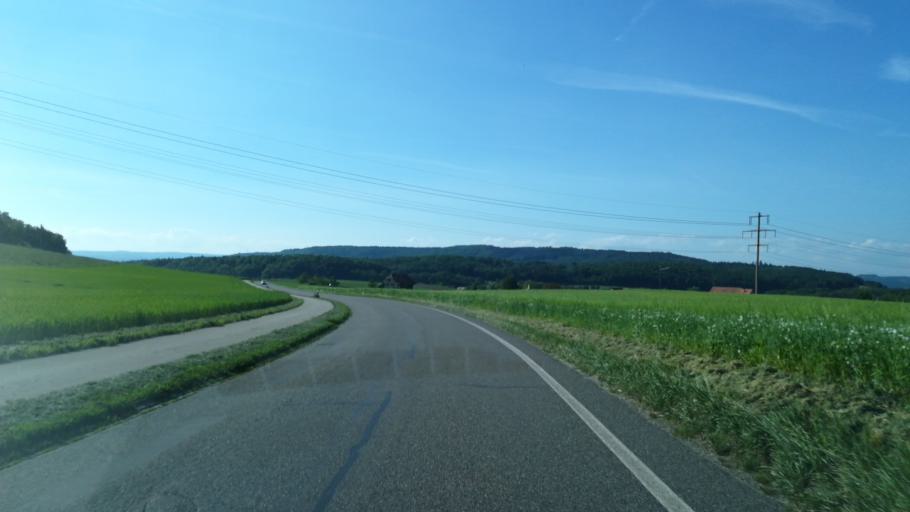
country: CH
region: Thurgau
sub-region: Frauenfeld District
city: Wagenhausen
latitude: 47.6675
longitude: 8.8139
